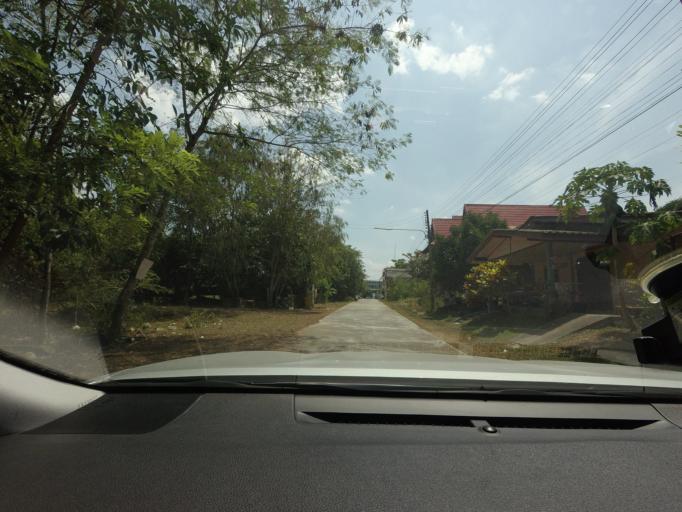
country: TH
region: Narathiwat
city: Rueso
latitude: 6.3809
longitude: 101.5090
